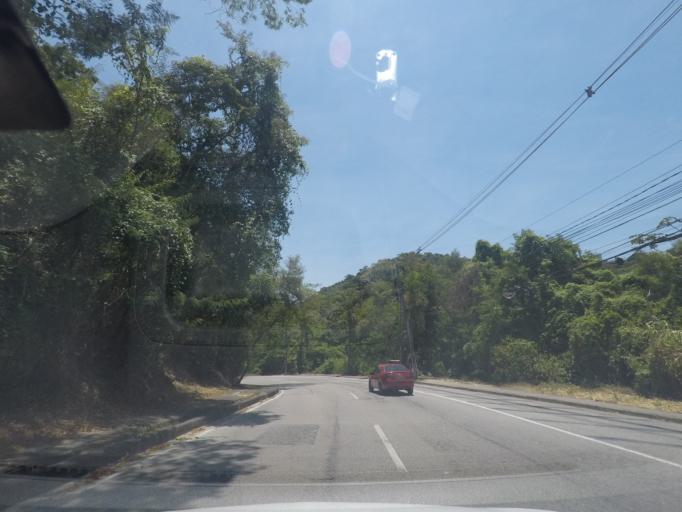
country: BR
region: Rio de Janeiro
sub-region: Niteroi
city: Niteroi
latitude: -22.9205
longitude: -43.0643
